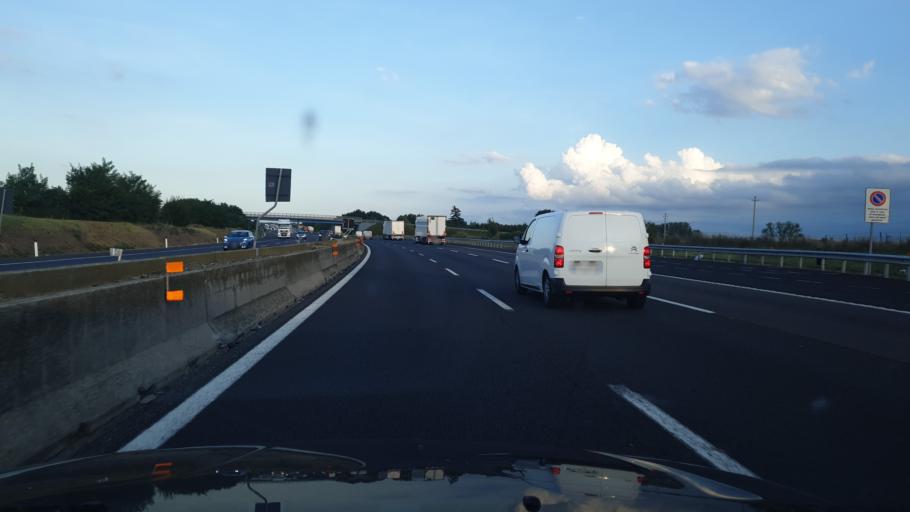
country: IT
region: Emilia-Romagna
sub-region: Provincia di Bologna
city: Toscanella
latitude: 44.4151
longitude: 11.6304
